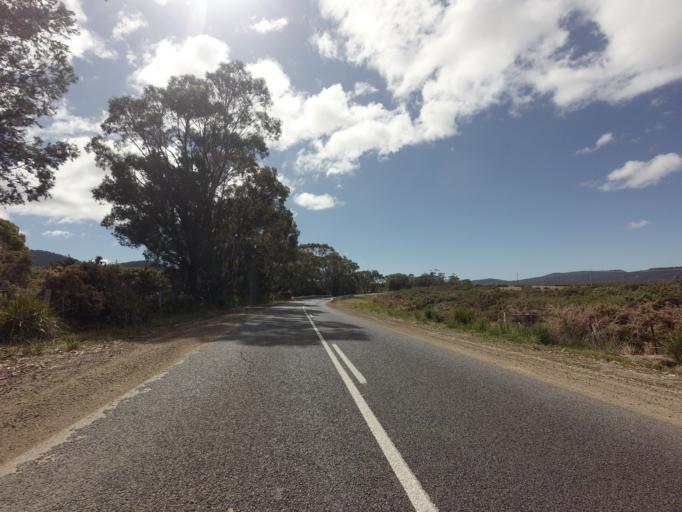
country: AU
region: Tasmania
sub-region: Break O'Day
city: St Helens
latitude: -41.9283
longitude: 148.2293
